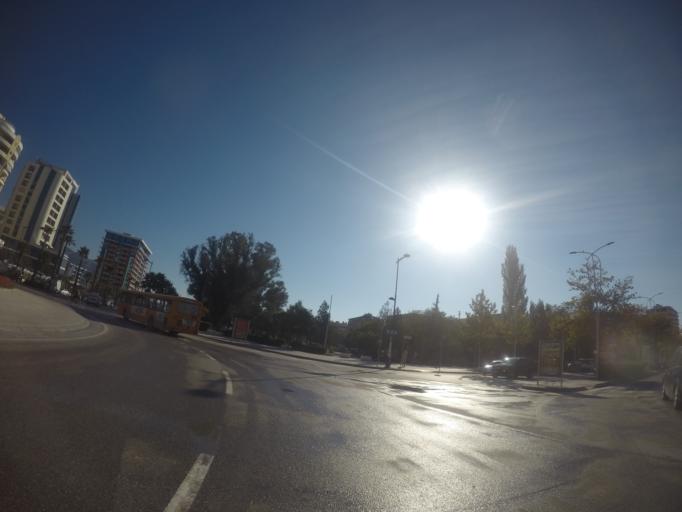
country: AL
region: Vlore
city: Vlore
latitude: 40.4547
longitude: 19.4863
